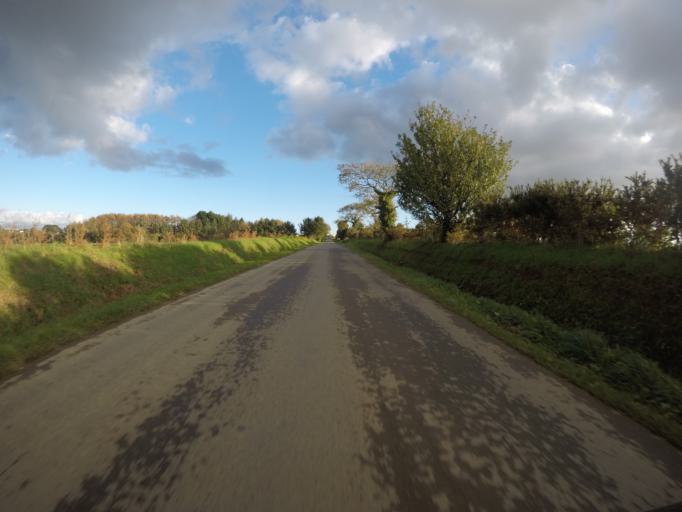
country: FR
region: Brittany
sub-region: Departement des Cotes-d'Armor
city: Louargat
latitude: 48.4671
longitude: -3.3088
